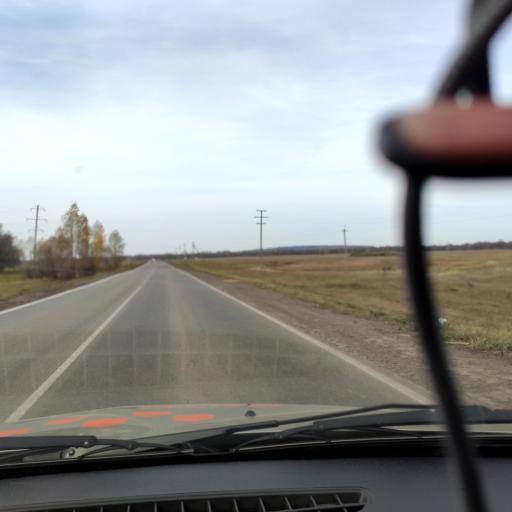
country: RU
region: Bashkortostan
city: Kabakovo
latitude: 54.5546
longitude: 56.0214
